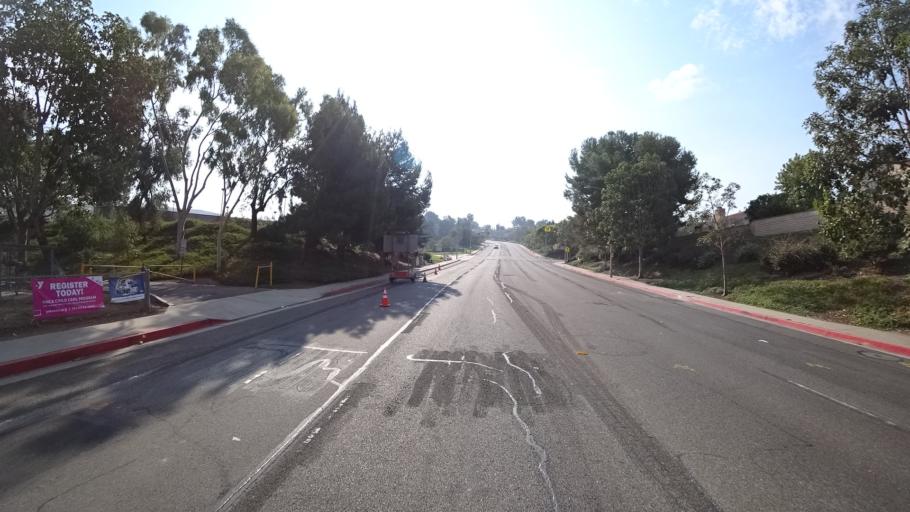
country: US
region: California
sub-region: Orange County
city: San Clemente
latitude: 33.4649
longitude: -117.6263
